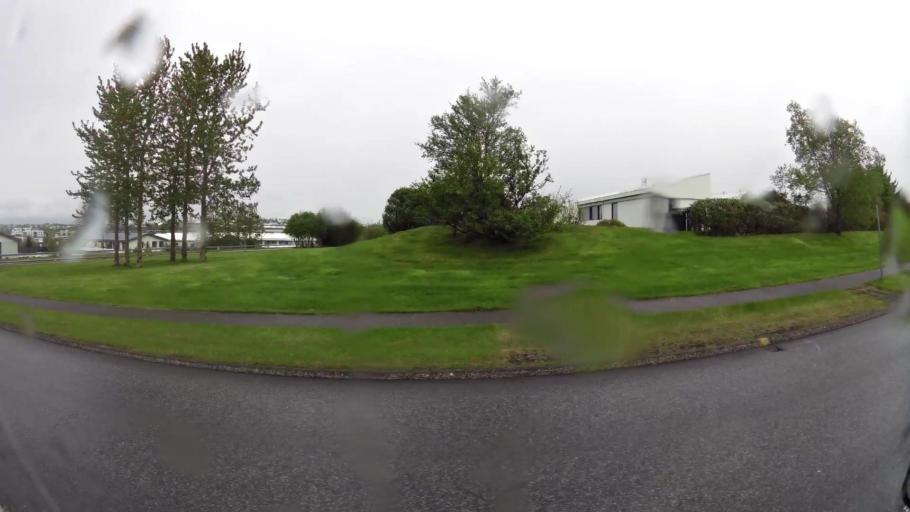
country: IS
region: Capital Region
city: Gardabaer
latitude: 64.0911
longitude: -21.9143
